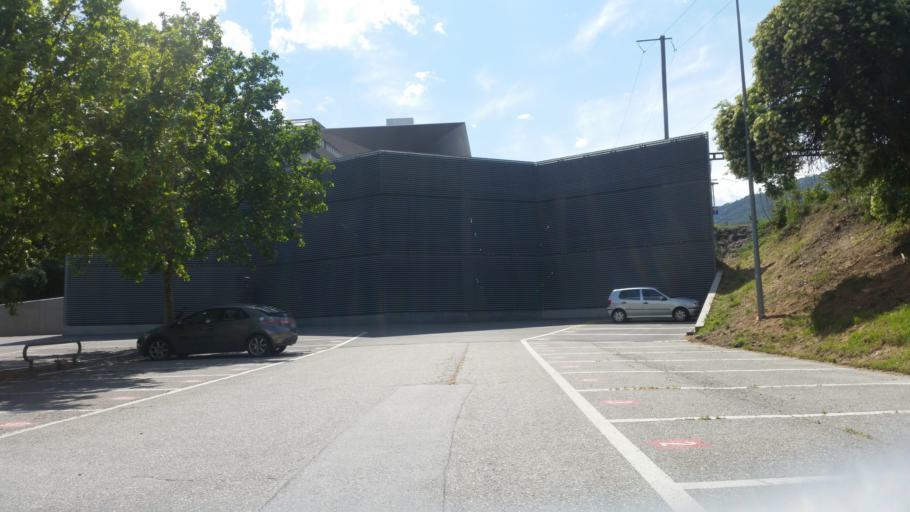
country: CH
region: Valais
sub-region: Sierre District
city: Sierre
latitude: 46.2918
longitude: 7.5336
